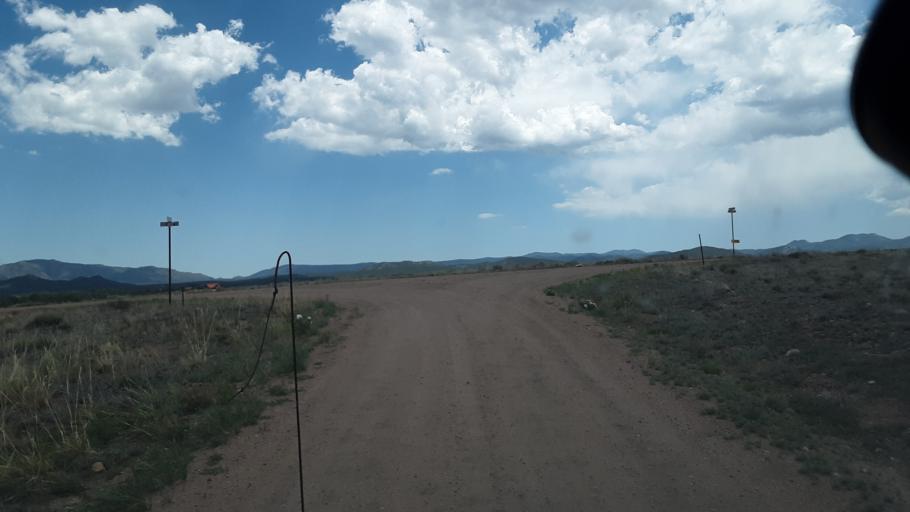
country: US
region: Colorado
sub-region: Custer County
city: Westcliffe
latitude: 38.2710
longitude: -105.4692
